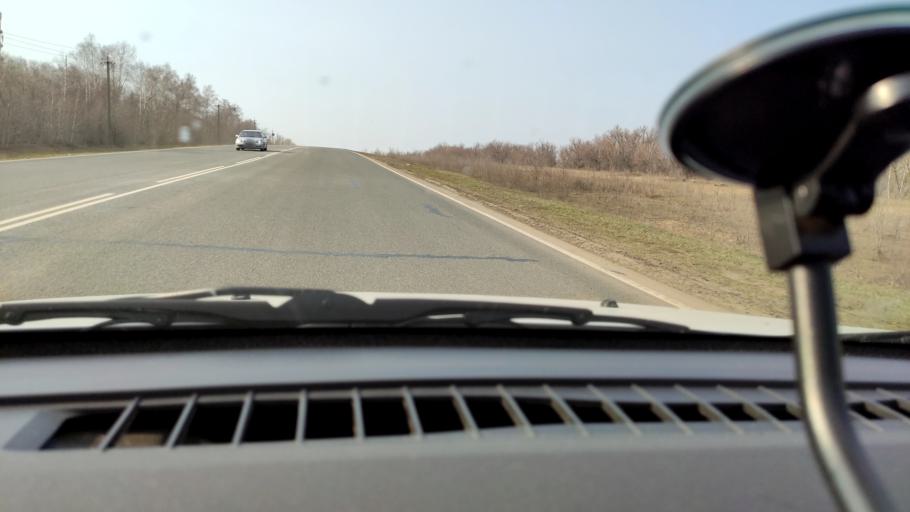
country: RU
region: Samara
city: Dubovyy Umet
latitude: 53.0751
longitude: 50.3562
